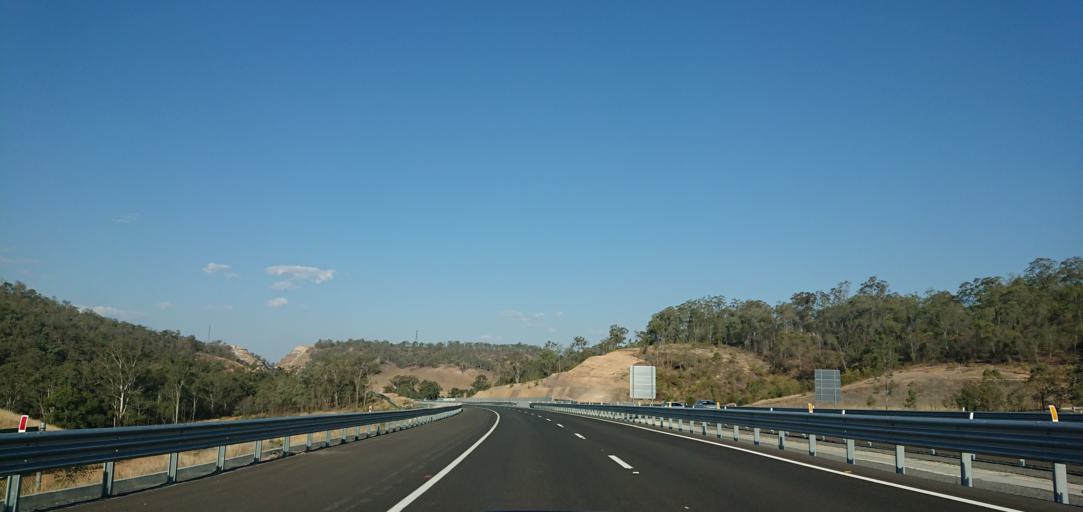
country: AU
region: Queensland
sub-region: Toowoomba
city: East Toowoomba
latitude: -27.5149
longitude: 152.0224
